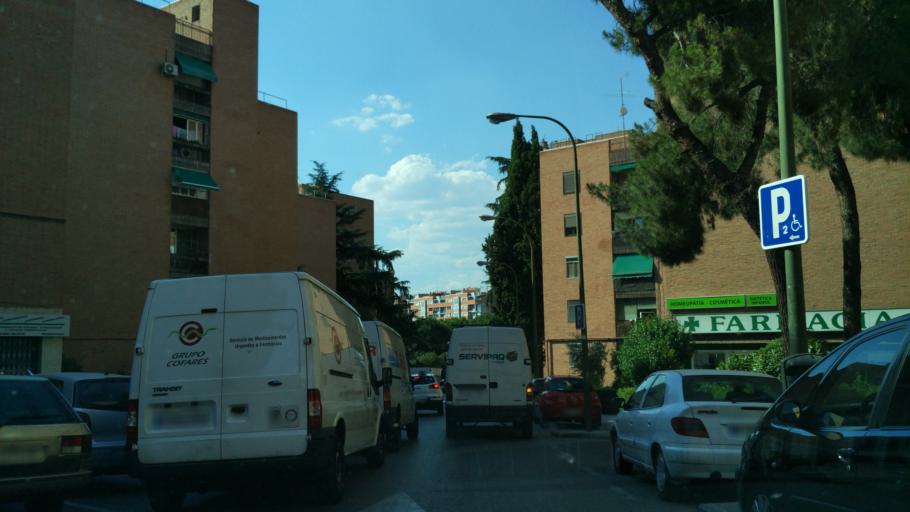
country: ES
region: Madrid
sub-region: Provincia de Madrid
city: Tetuan de las Victorias
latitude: 40.4701
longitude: -3.7221
